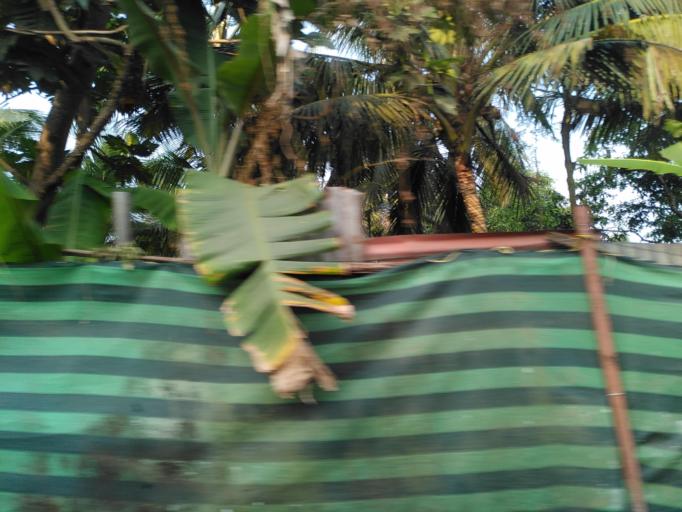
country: IN
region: Kerala
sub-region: Alappuzha
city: Arukutti
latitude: 9.9279
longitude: 76.3276
